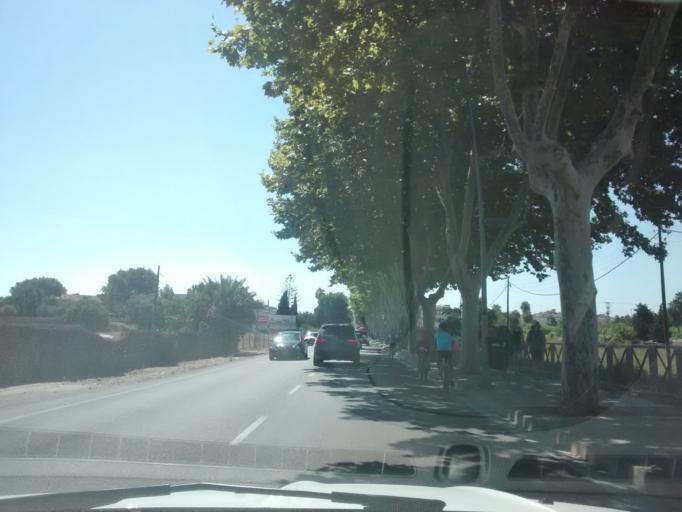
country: ES
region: Balearic Islands
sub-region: Illes Balears
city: Port d'Alcudia
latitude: 39.8479
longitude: 3.1292
